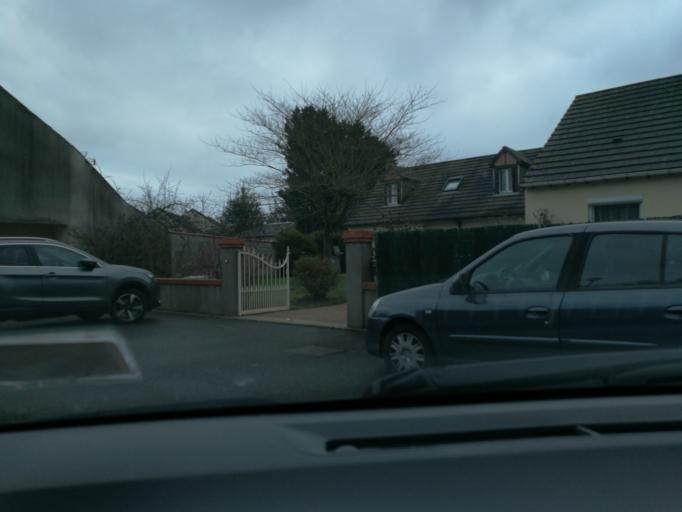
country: FR
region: Centre
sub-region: Departement du Loiret
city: Fleury-les-Aubrais
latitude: 47.9383
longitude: 1.9277
